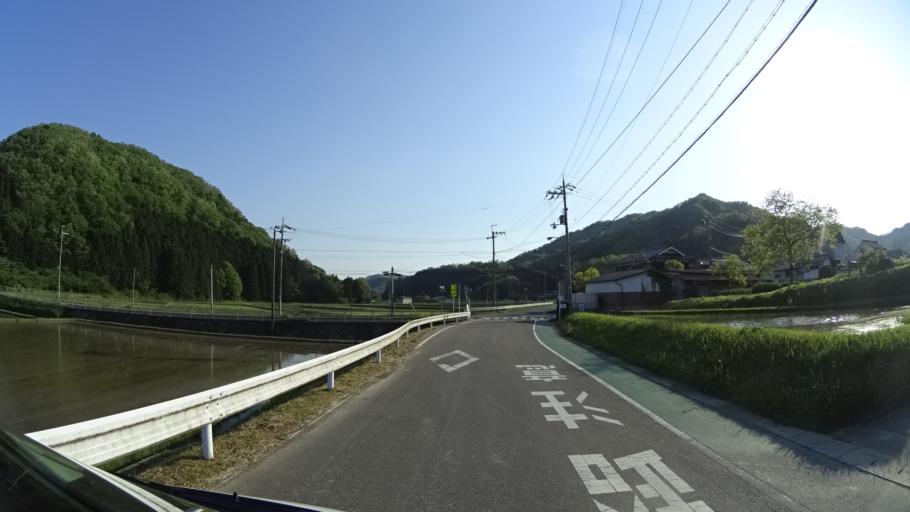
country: JP
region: Kyoto
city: Kameoka
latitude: 35.1417
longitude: 135.4197
